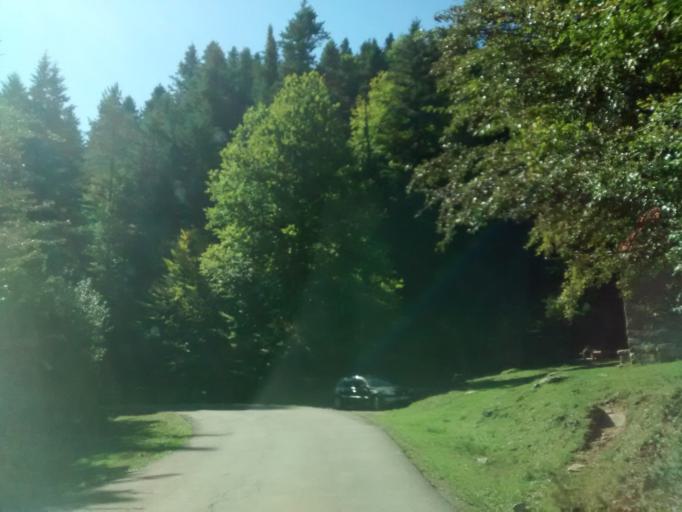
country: ES
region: Aragon
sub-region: Provincia de Huesca
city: Aragues del Puerto
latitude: 42.8307
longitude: -0.7124
